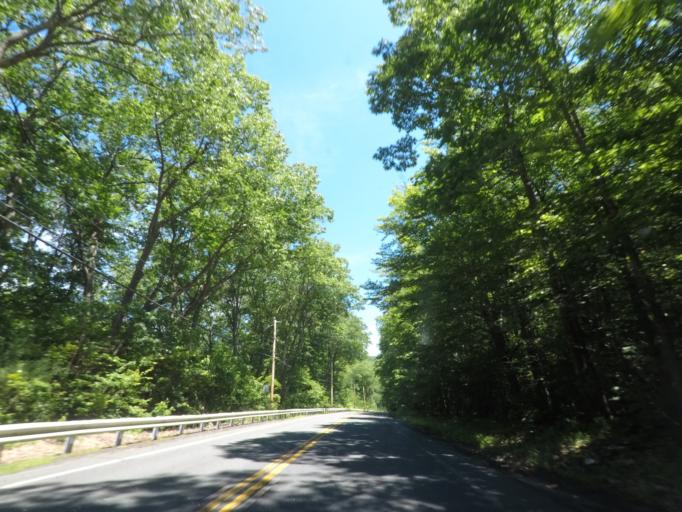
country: US
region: Massachusetts
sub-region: Berkshire County
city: Becket
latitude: 42.2564
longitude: -72.9447
